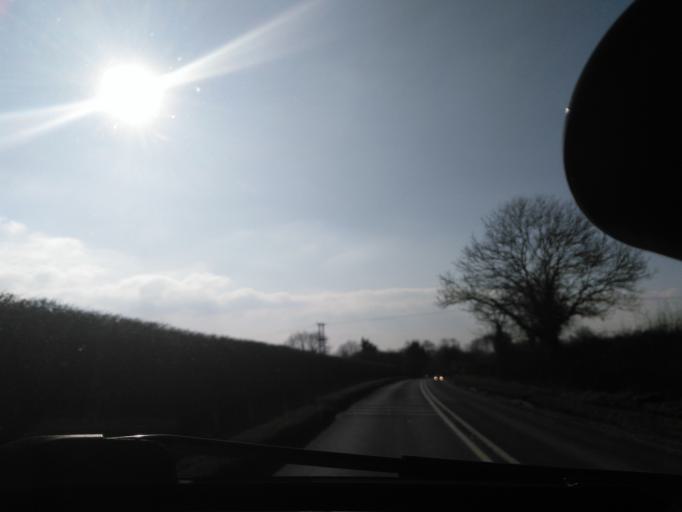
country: GB
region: England
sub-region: Wiltshire
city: Malmesbury
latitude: 51.5589
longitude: -2.1063
